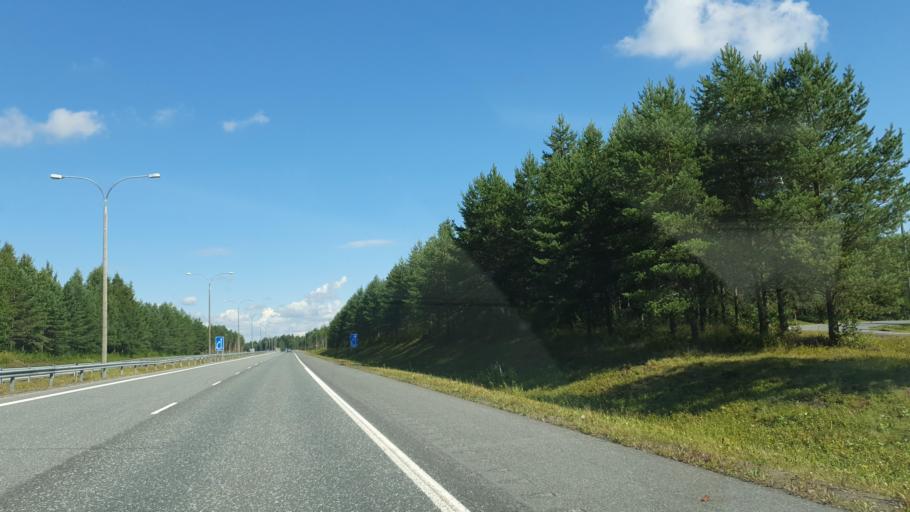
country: FI
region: Northern Savo
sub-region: Ylae-Savo
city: Iisalmi
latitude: 63.5464
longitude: 27.2511
